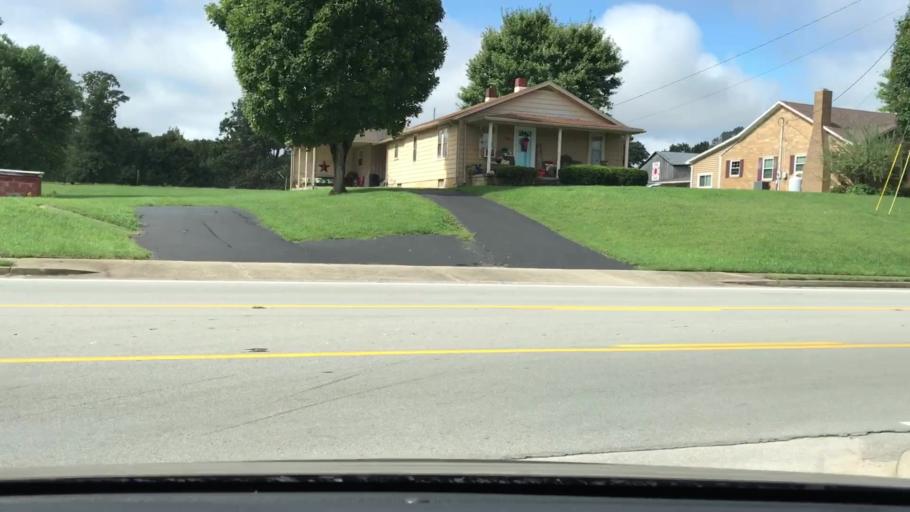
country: US
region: Kentucky
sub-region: Russell County
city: Jamestown
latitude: 36.9944
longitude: -85.0710
